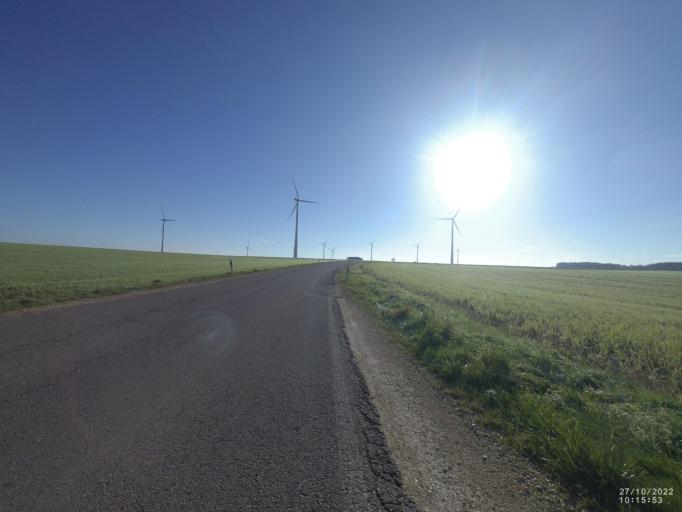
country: DE
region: Baden-Wuerttemberg
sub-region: Regierungsbezirk Stuttgart
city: Bohmenkirch
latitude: 48.6614
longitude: 9.9223
